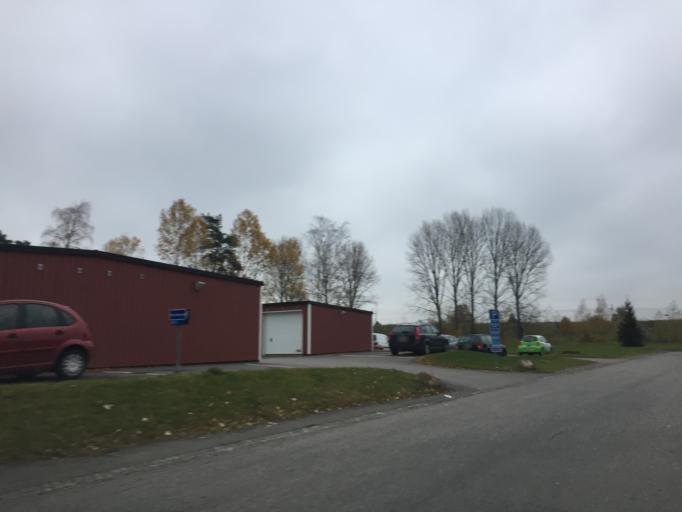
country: SE
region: Vaestra Goetaland
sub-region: Trollhattan
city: Trollhattan
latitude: 58.2698
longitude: 12.3125
